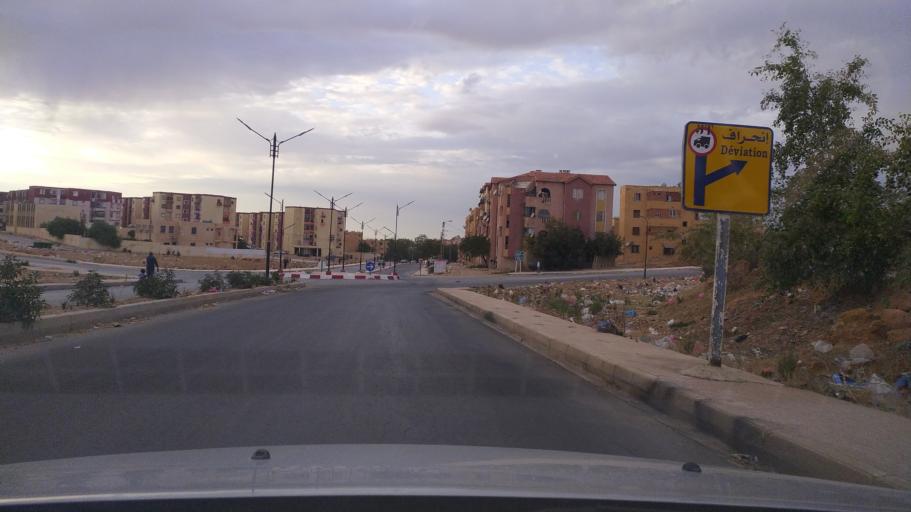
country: DZ
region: Tiaret
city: Frenda
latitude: 35.0534
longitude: 1.0629
